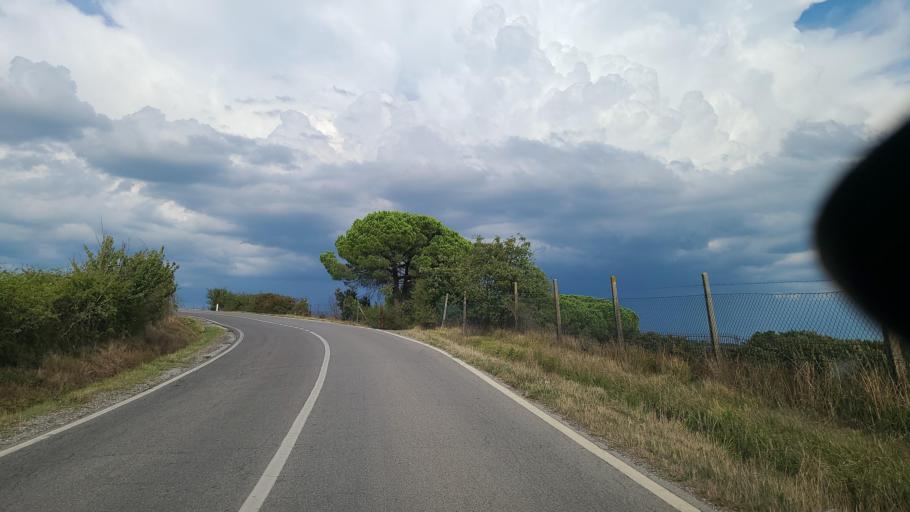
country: IT
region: Tuscany
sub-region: Province of Florence
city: Gambassi Terme
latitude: 43.4813
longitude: 10.9599
